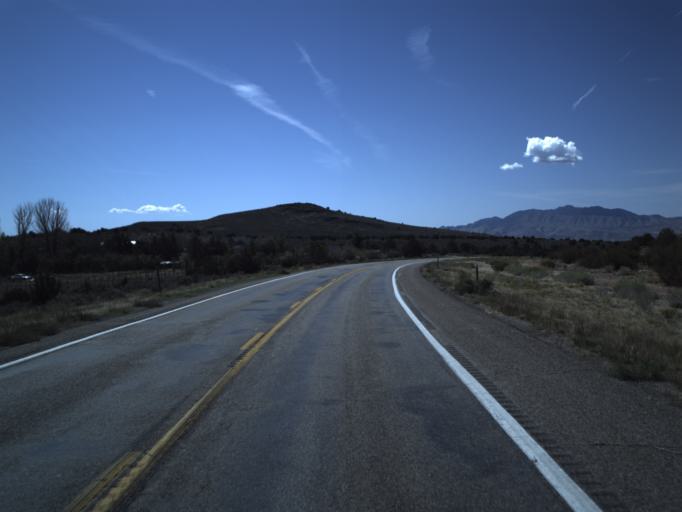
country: US
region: Utah
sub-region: Washington County
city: Ivins
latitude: 37.3647
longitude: -113.6679
